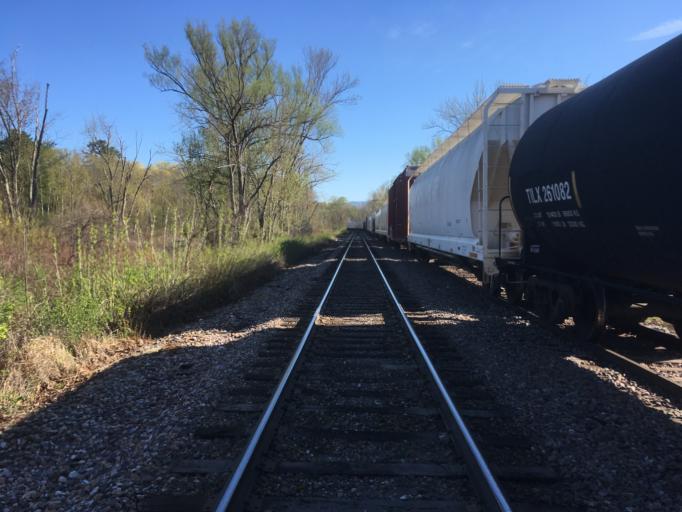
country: US
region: Vermont
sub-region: Rutland County
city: West Rutland
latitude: 43.6555
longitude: -73.0357
